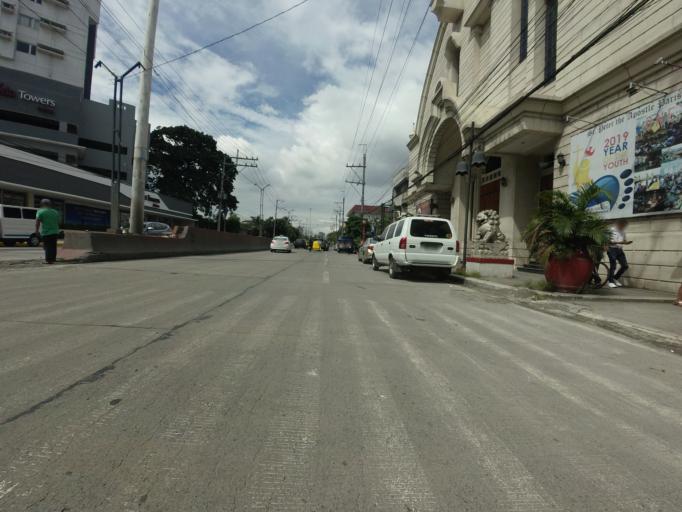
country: PH
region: Metro Manila
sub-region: City of Manila
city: Quiapo
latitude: 14.5835
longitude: 120.9963
